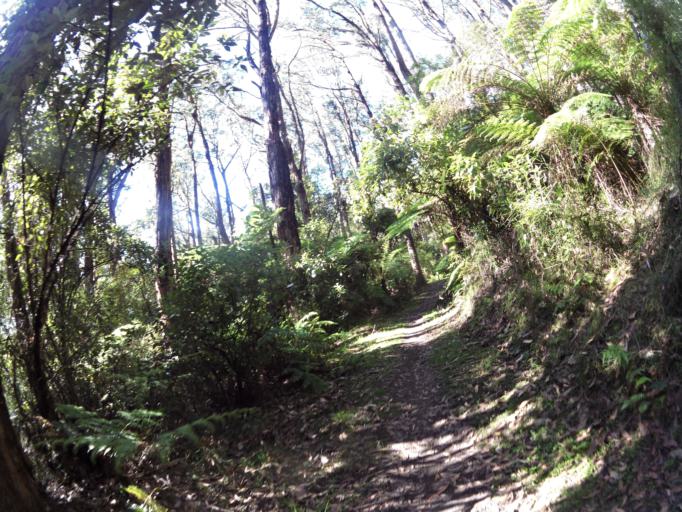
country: AU
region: Victoria
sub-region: Colac-Otway
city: Apollo Bay
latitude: -38.5497
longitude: 143.7398
